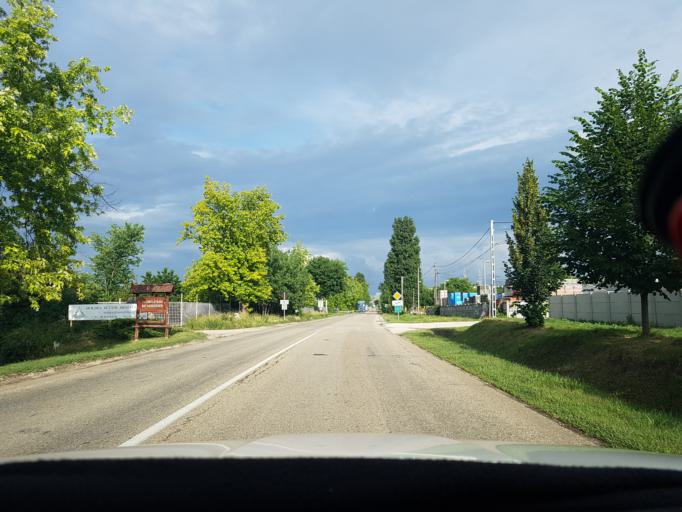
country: HU
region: Komarom-Esztergom
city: Sutto
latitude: 47.7561
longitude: 18.4597
